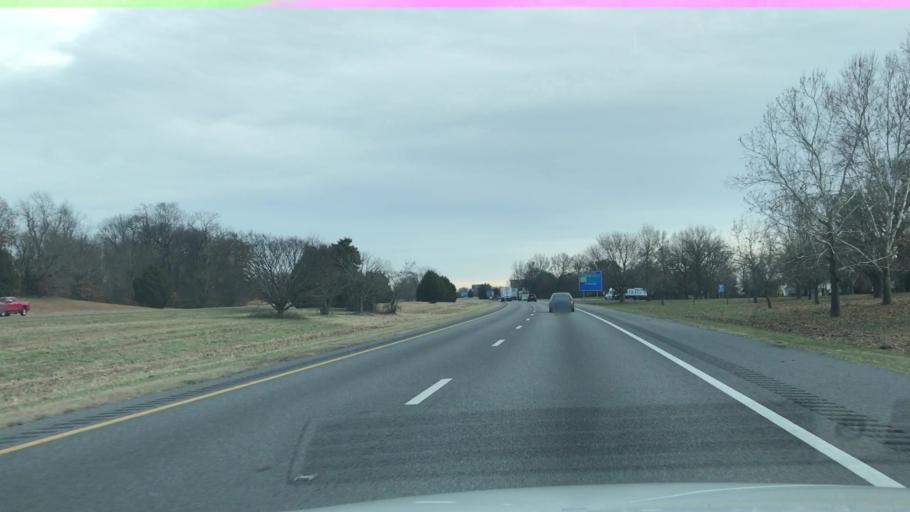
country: US
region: Tennessee
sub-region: Montgomery County
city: Clarksville
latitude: 36.6371
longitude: -87.3342
